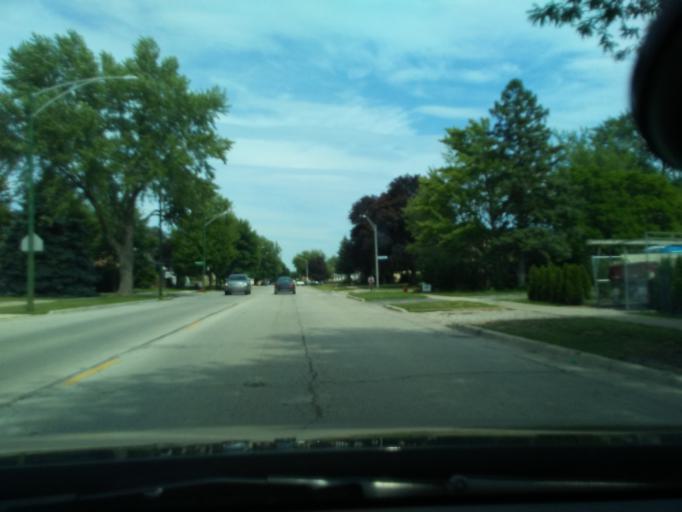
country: US
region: Illinois
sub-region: Cook County
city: Norridge
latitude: 41.9741
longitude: -87.8225
